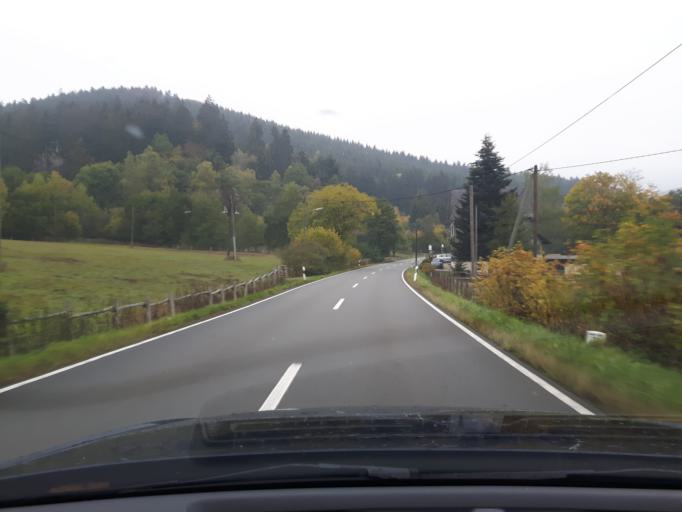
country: DE
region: North Rhine-Westphalia
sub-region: Regierungsbezirk Arnsberg
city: Bad Laasphe
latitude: 50.9460
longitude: 8.3907
